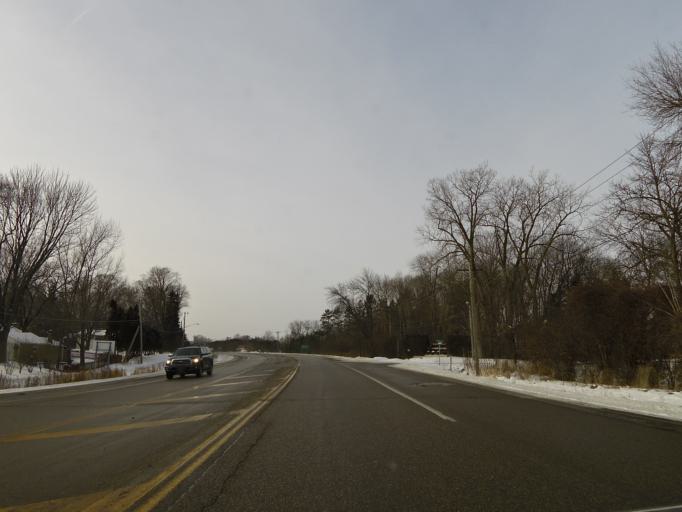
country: US
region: Minnesota
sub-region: Hennepin County
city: Shorewood
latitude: 44.8915
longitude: -93.6077
